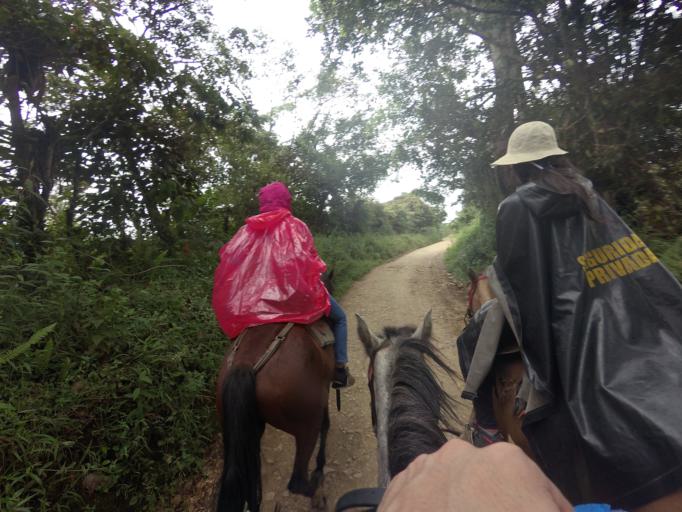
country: CO
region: Huila
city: San Agustin
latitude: 1.9036
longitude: -76.2933
